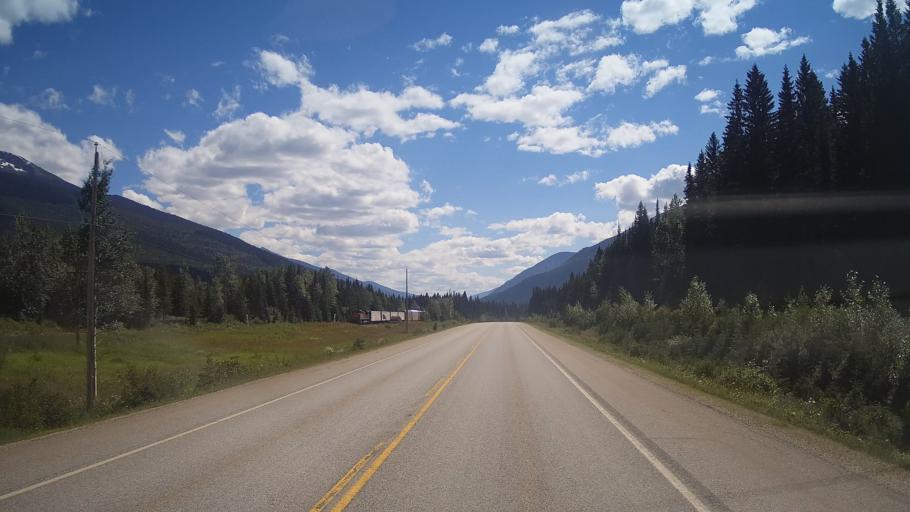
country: CA
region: Alberta
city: Jasper Park Lodge
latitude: 52.5774
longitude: -119.0973
